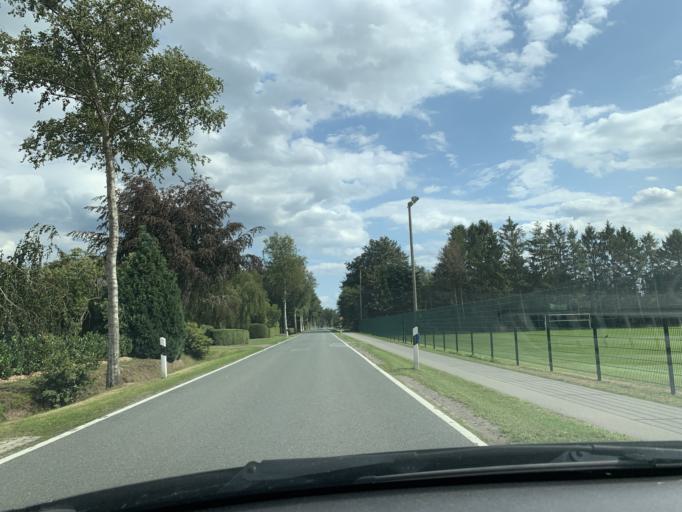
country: DE
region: Lower Saxony
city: Apen
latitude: 53.2706
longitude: 7.8287
